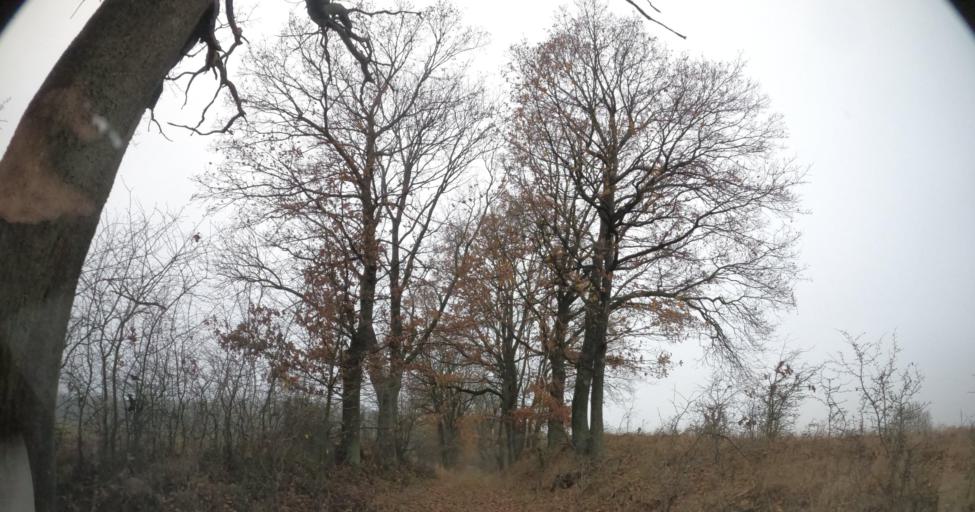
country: PL
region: West Pomeranian Voivodeship
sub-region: Powiat drawski
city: Drawsko Pomorskie
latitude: 53.5956
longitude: 15.7803
